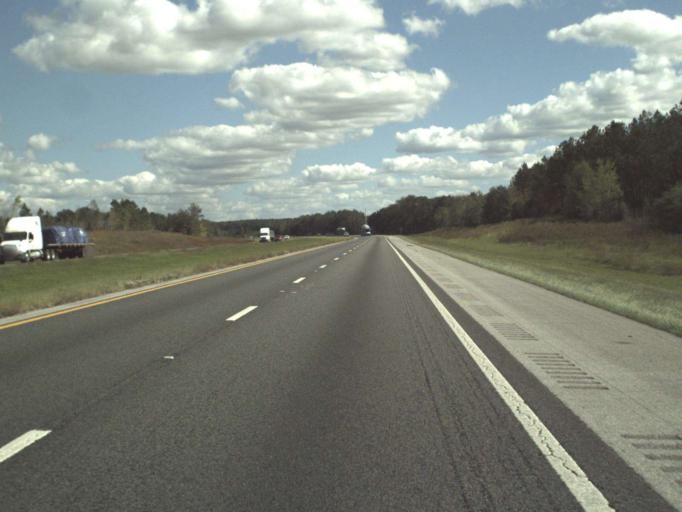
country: US
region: Florida
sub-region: Jackson County
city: Marianna
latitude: 30.6873
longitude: -85.1123
